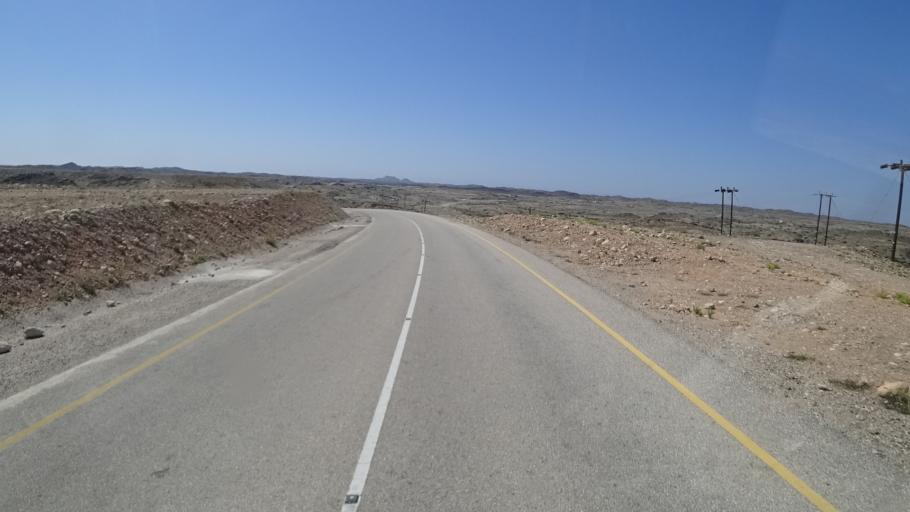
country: OM
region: Zufar
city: Salalah
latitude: 17.0856
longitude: 54.9264
